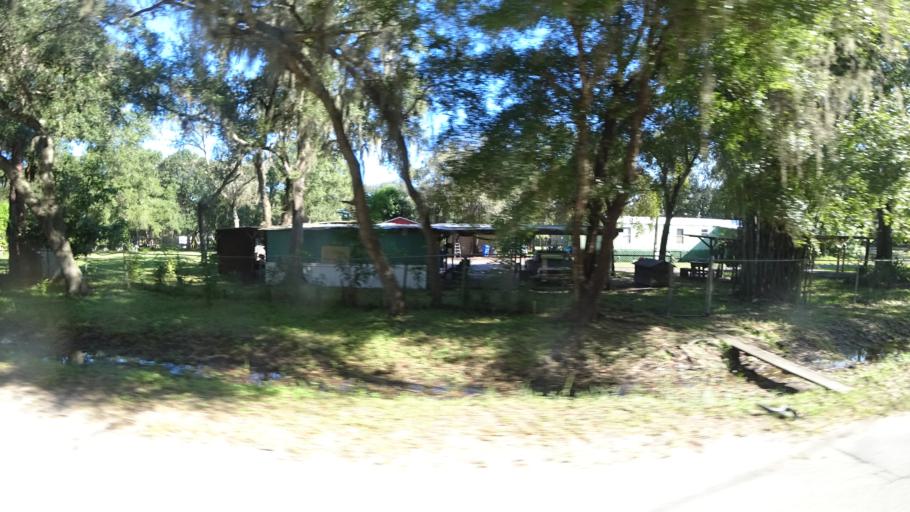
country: US
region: Florida
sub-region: Hillsborough County
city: Sun City Center
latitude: 27.6578
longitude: -82.3635
